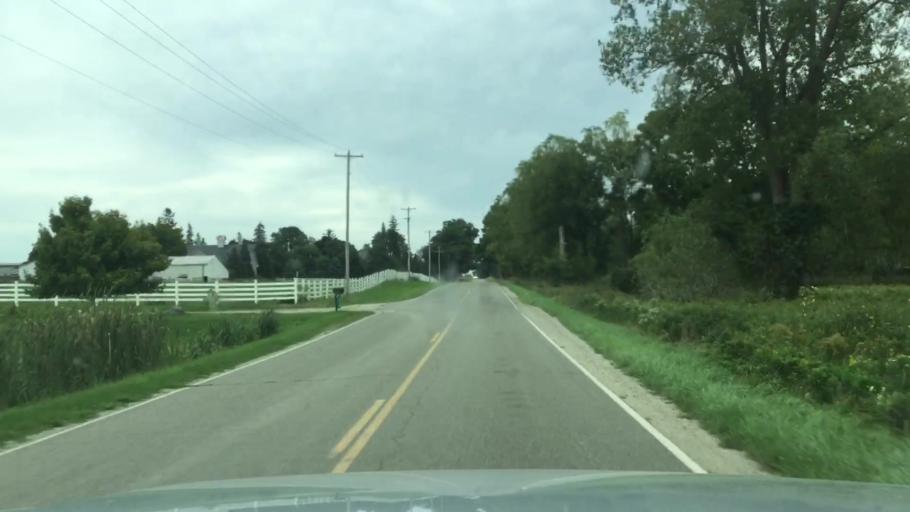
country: US
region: Michigan
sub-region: Shiawassee County
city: Durand
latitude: 42.8231
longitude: -83.9890
